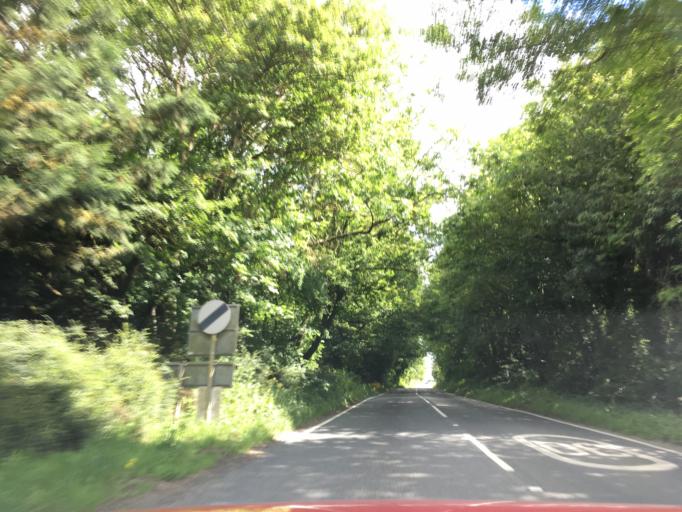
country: GB
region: England
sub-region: Oxfordshire
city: Burford
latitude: 51.8172
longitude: -1.6230
